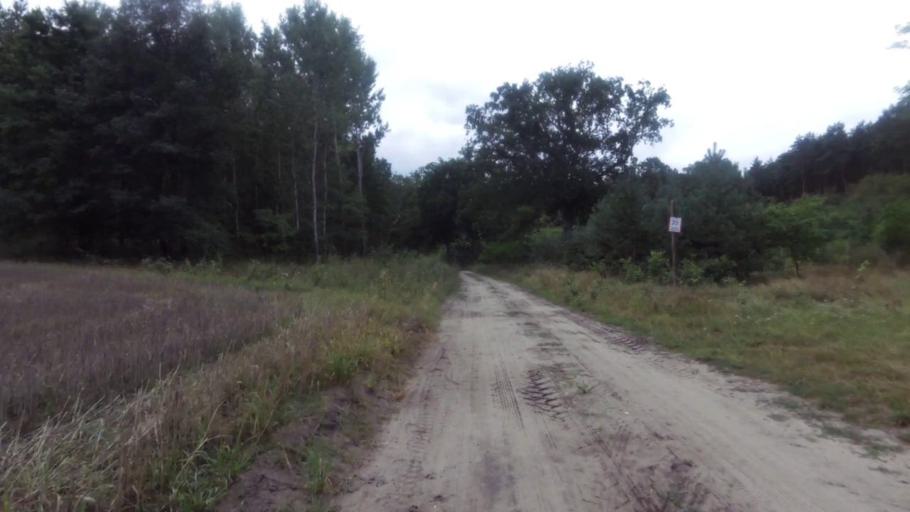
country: PL
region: West Pomeranian Voivodeship
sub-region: Powiat mysliborski
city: Boleszkowice
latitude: 52.6712
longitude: 14.6163
